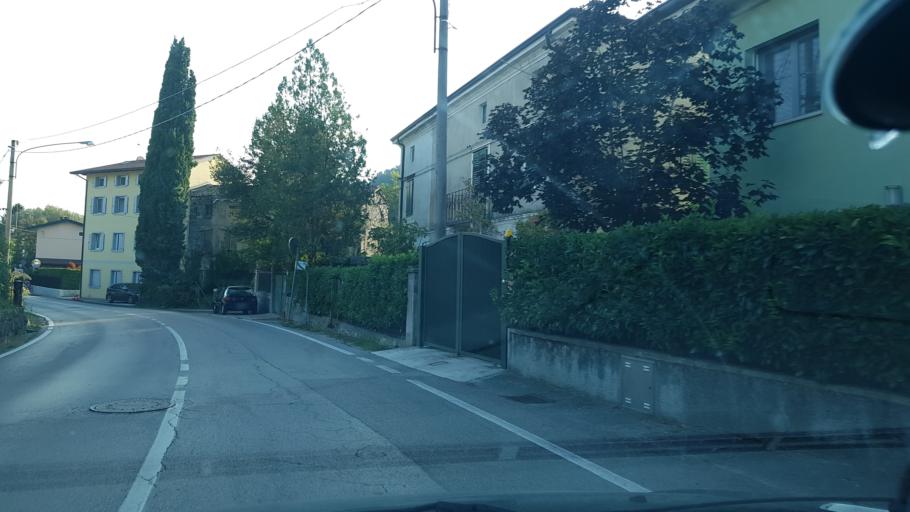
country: IT
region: Friuli Venezia Giulia
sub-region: Provincia di Gorizia
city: Gorizia
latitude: 45.9642
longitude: 13.6154
